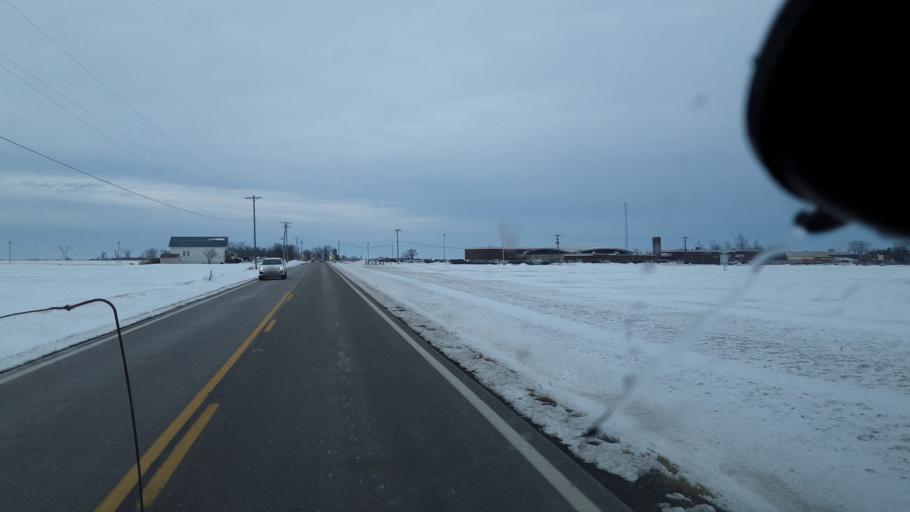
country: US
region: Ohio
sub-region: Pickaway County
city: Williamsport
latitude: 39.6581
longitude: -83.1233
